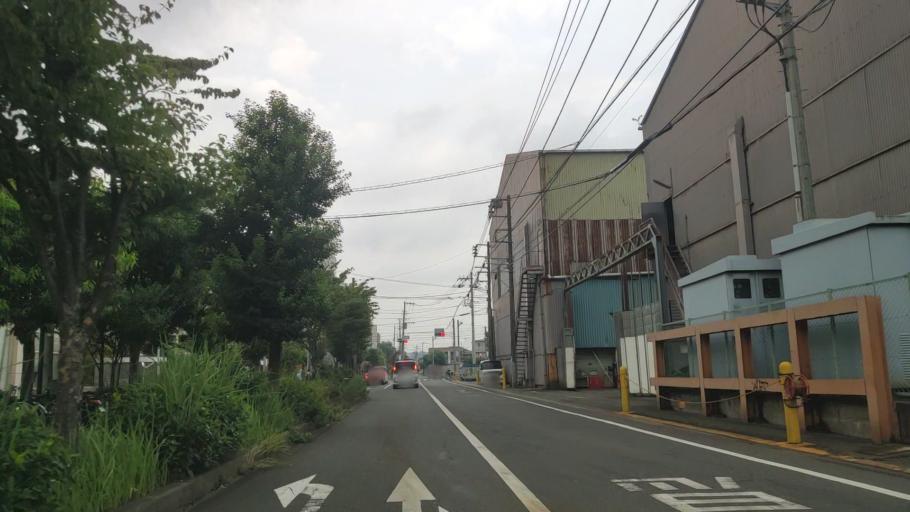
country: JP
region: Kanagawa
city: Minami-rinkan
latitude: 35.4909
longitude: 139.4579
